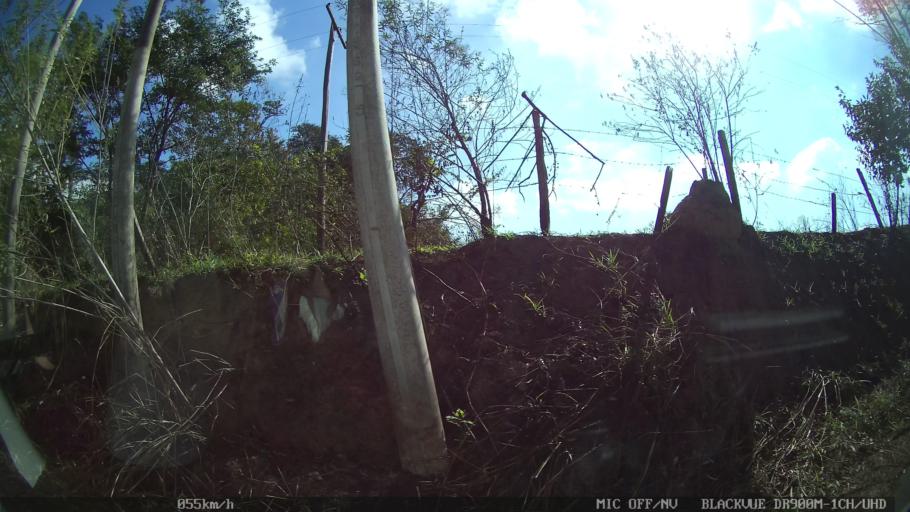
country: BR
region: Sao Paulo
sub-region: Indaiatuba
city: Indaiatuba
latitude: -22.9940
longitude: -47.1852
